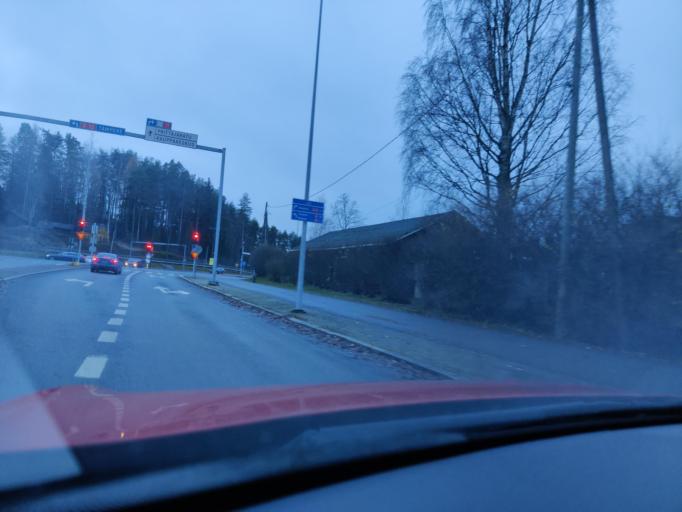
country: FI
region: Pirkanmaa
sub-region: Tampere
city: Nokia
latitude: 61.4809
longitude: 23.5293
